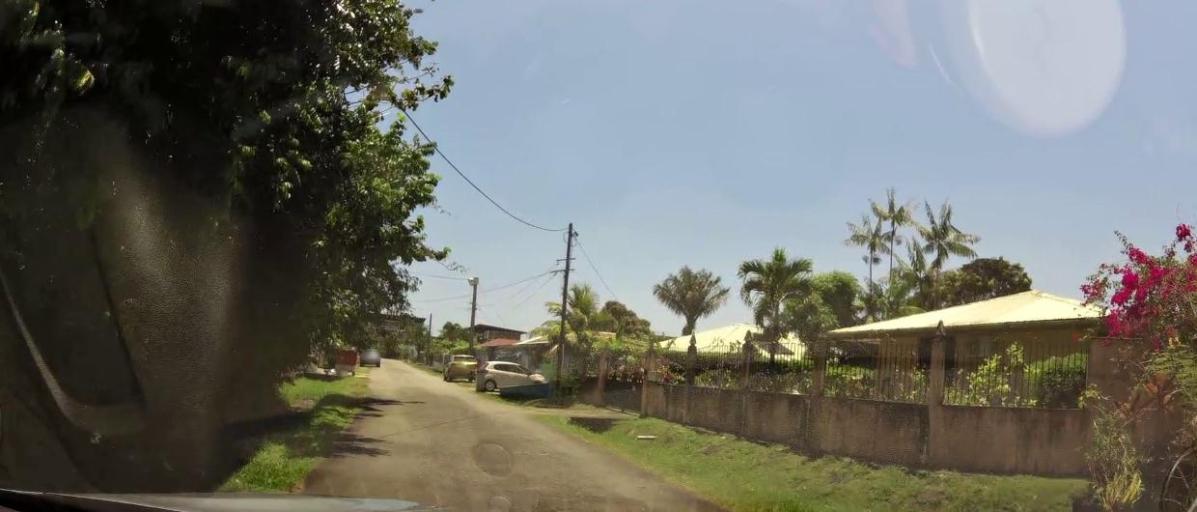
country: GF
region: Guyane
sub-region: Guyane
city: Cayenne
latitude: 4.9348
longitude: -52.3047
